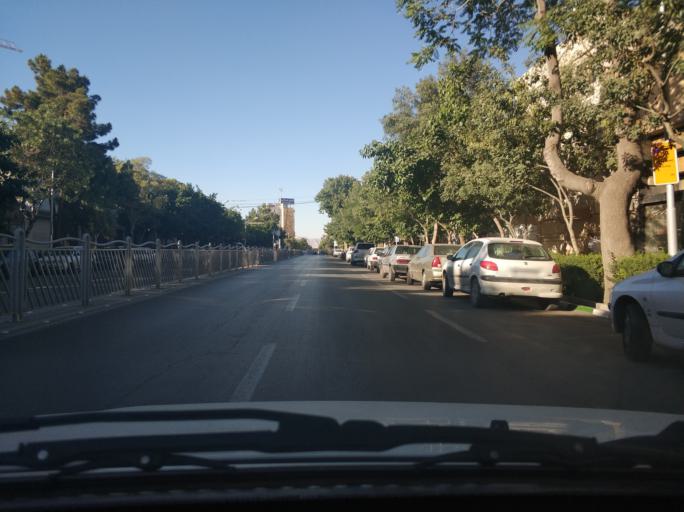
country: IR
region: Razavi Khorasan
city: Mashhad
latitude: 36.2928
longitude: 59.6088
